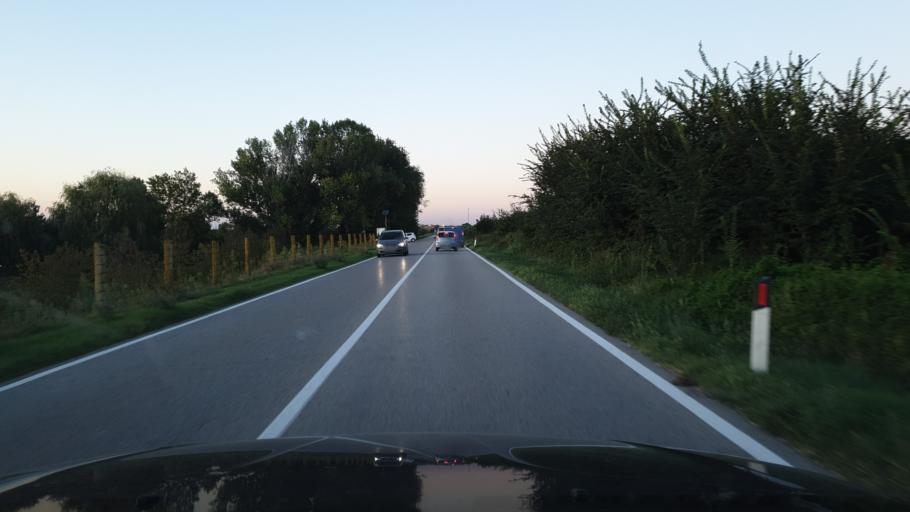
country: IT
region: Emilia-Romagna
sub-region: Provincia di Bologna
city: Ca De Fabbri
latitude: 44.6087
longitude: 11.4457
